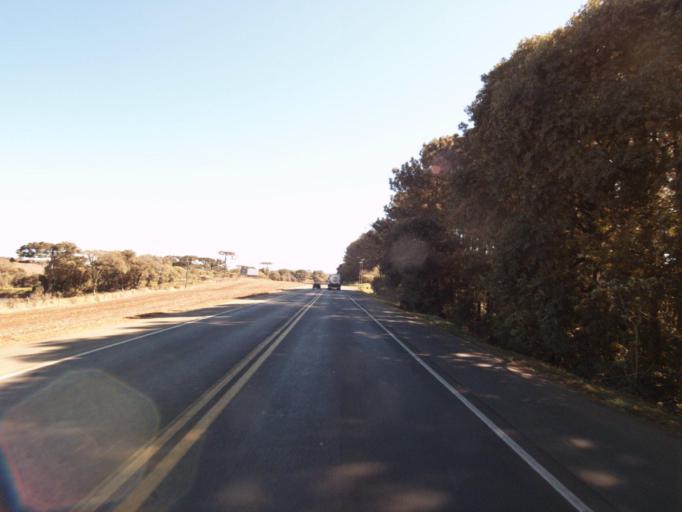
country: BR
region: Santa Catarina
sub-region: Xanxere
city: Xanxere
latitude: -26.8719
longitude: -52.2989
